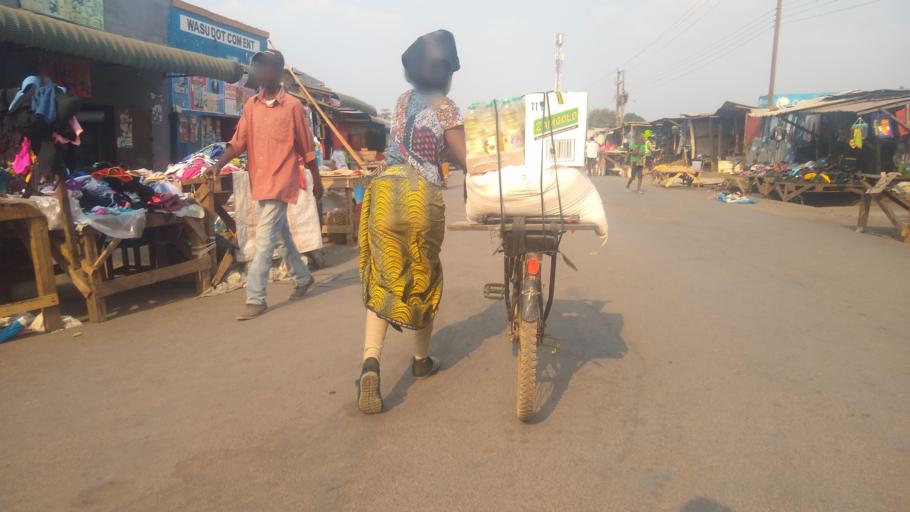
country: ZM
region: Lusaka
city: Lusaka
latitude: -15.4473
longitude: 28.3793
